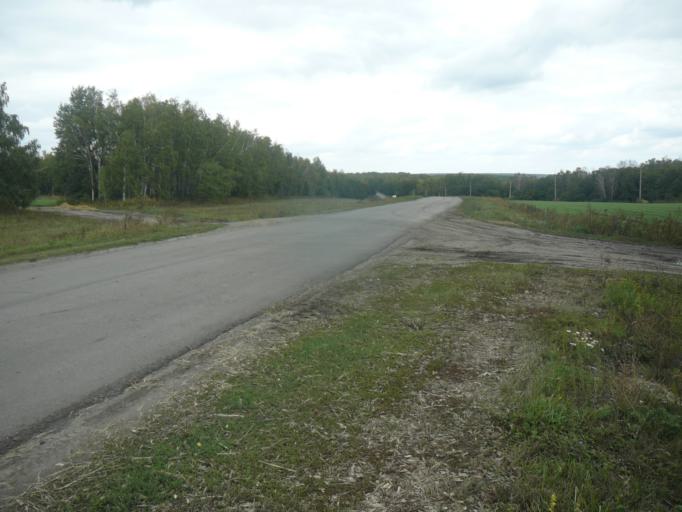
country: RU
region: Saratov
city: Svetlyy
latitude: 51.9457
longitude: 45.5895
